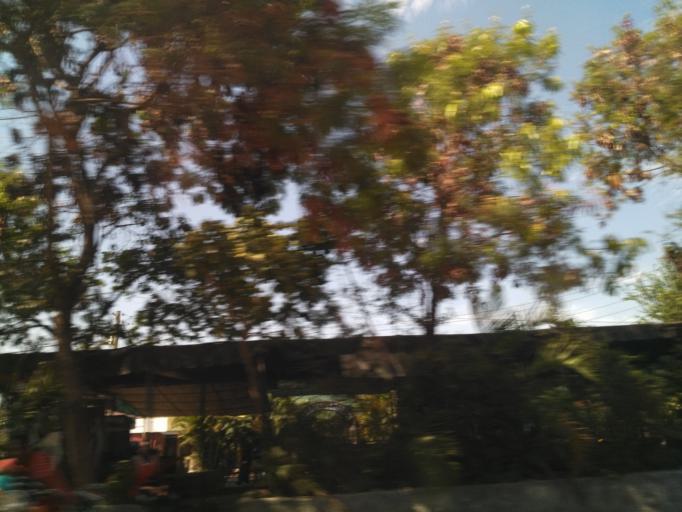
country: TZ
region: Mwanza
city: Mwanza
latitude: -2.4916
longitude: 32.9036
